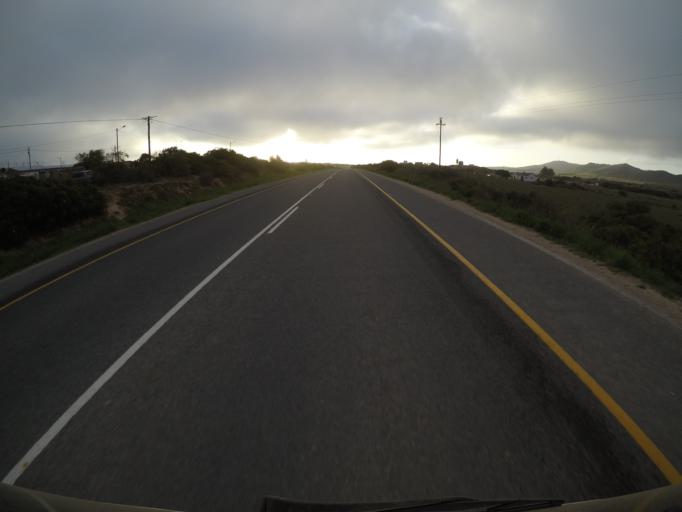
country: ZA
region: Western Cape
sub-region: Eden District Municipality
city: Mossel Bay
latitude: -34.1147
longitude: 22.0863
